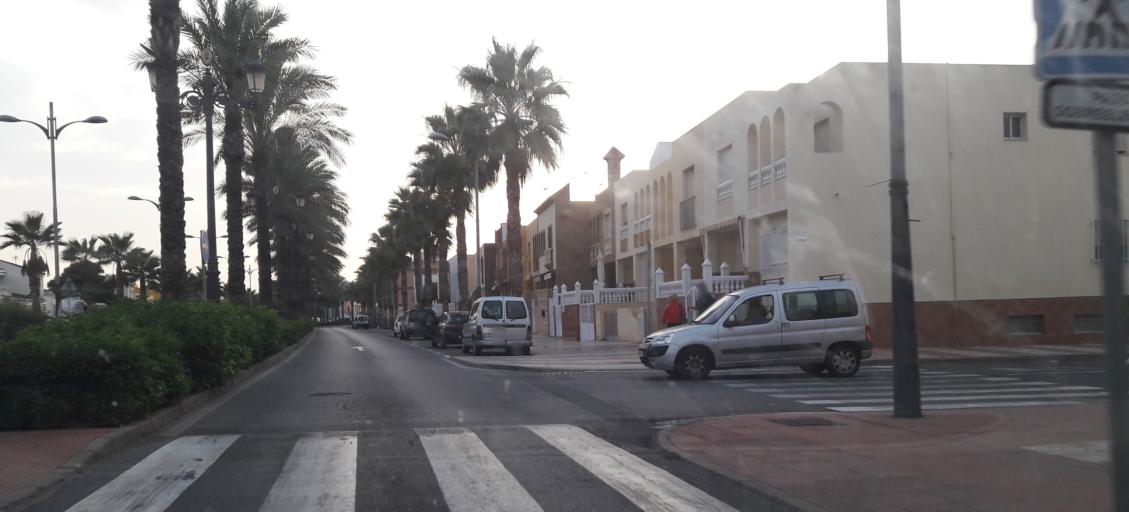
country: ES
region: Andalusia
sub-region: Provincia de Almeria
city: Roquetas de Mar
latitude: 36.7334
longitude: -2.6248
